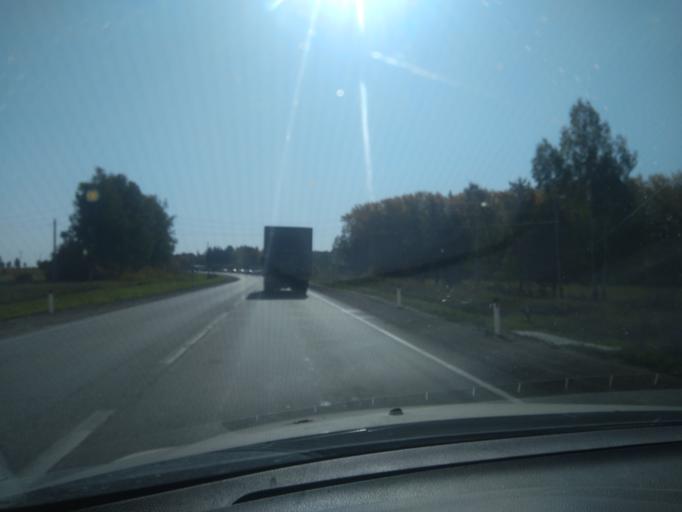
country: RU
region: Sverdlovsk
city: Sovkhoznyy
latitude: 56.6059
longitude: 61.3014
